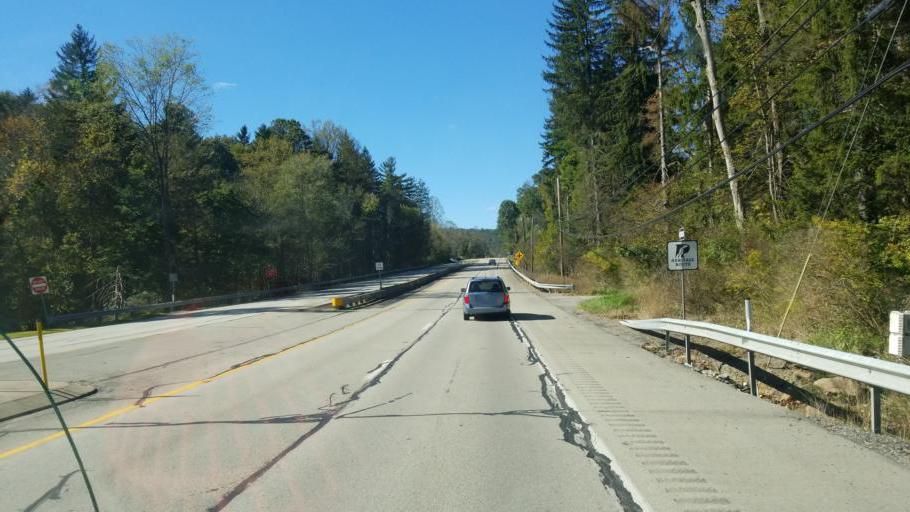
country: US
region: Pennsylvania
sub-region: Westmoreland County
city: Ligonier
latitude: 40.2641
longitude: -79.2798
